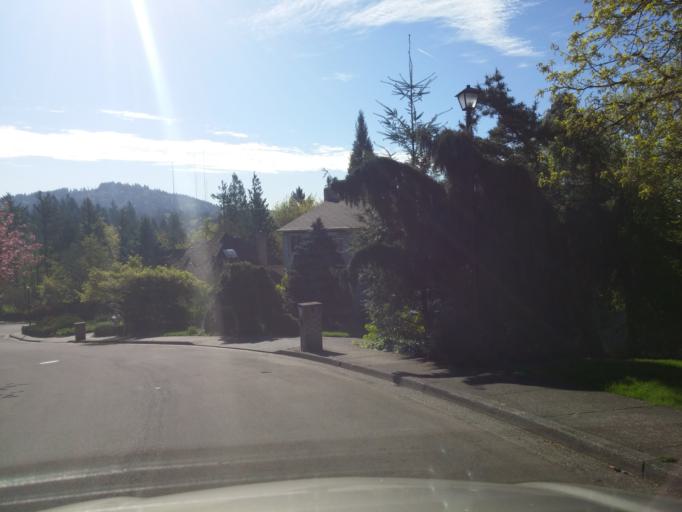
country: US
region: Oregon
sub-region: Washington County
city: Cedar Mill
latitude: 45.5345
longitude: -122.7879
